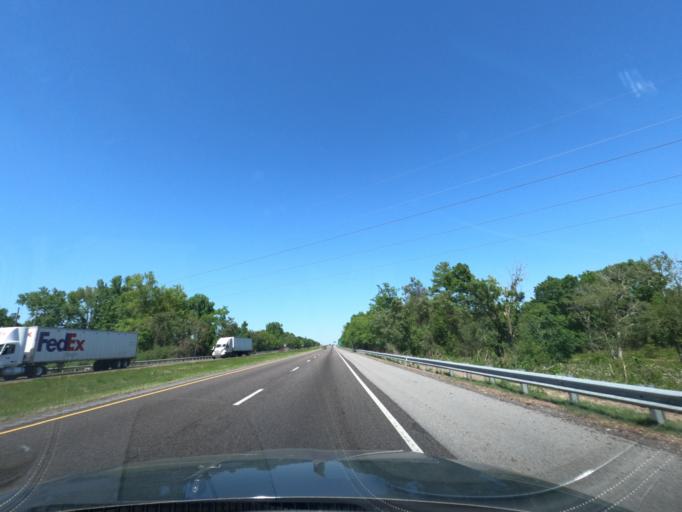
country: US
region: Georgia
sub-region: Richmond County
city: Augusta
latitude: 33.4408
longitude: -81.9404
